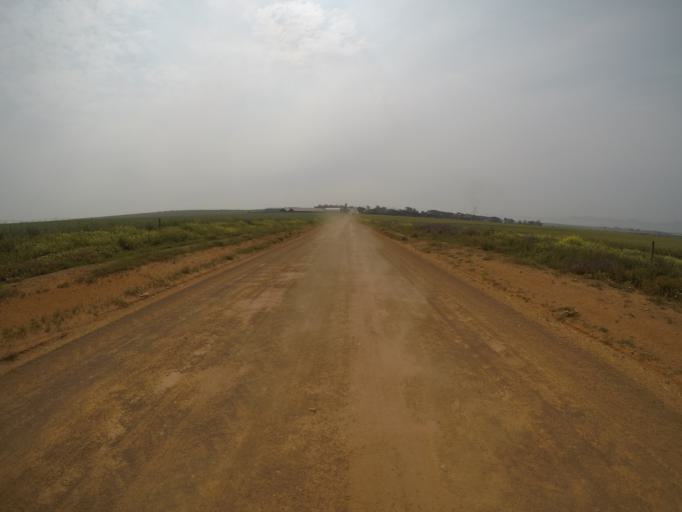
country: ZA
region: Western Cape
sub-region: City of Cape Town
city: Kraaifontein
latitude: -33.7103
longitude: 18.6877
